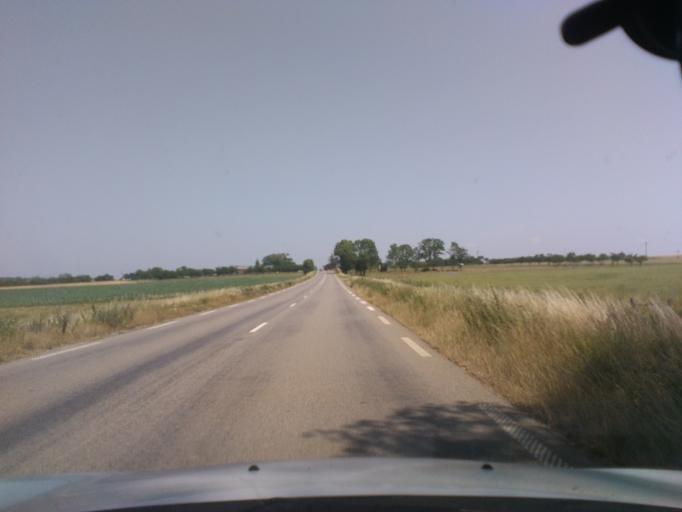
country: FR
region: Lorraine
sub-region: Departement des Vosges
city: Vittel
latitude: 48.3092
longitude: 5.9637
